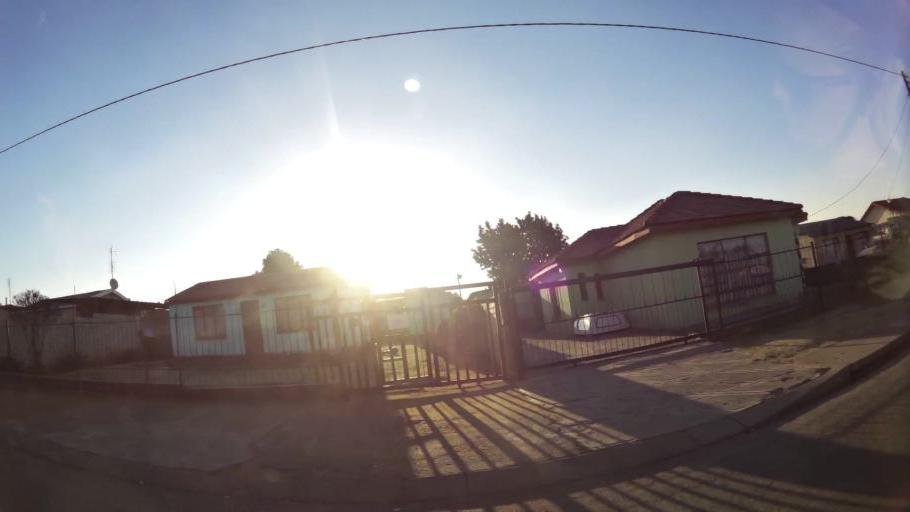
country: ZA
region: North-West
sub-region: Bojanala Platinum District Municipality
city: Rustenburg
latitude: -25.6320
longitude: 27.2102
